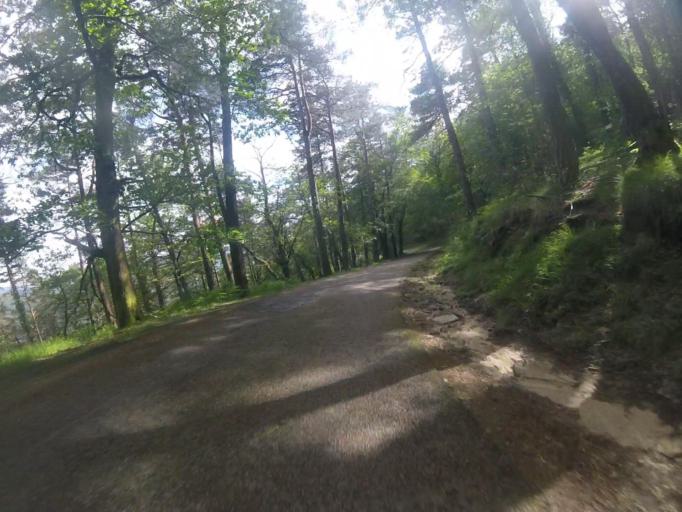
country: ES
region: Navarre
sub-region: Provincia de Navarra
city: Arantza
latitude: 43.2260
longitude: -1.8004
